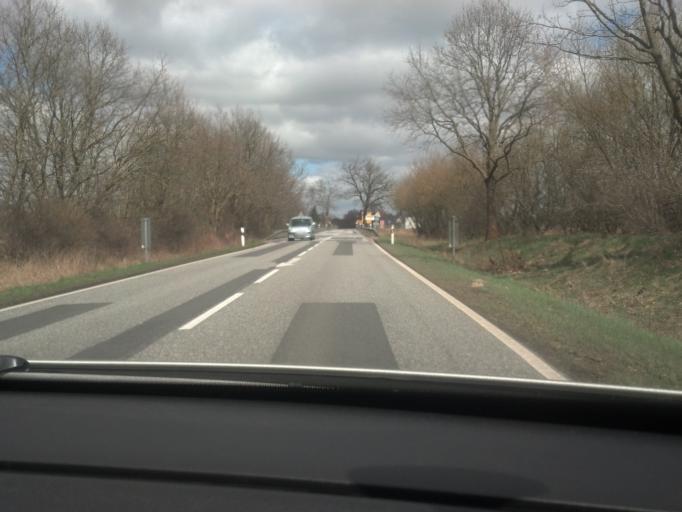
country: DE
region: Mecklenburg-Vorpommern
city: Plau am See
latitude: 53.3780
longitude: 12.2475
